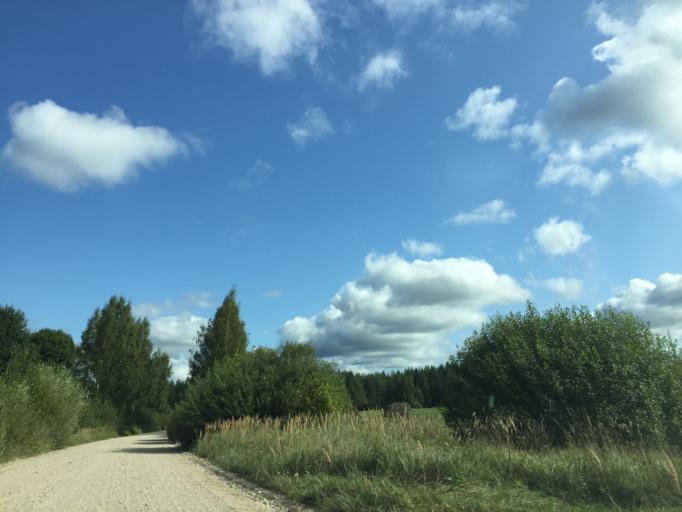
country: LV
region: Pargaujas
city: Stalbe
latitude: 57.3928
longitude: 24.9830
